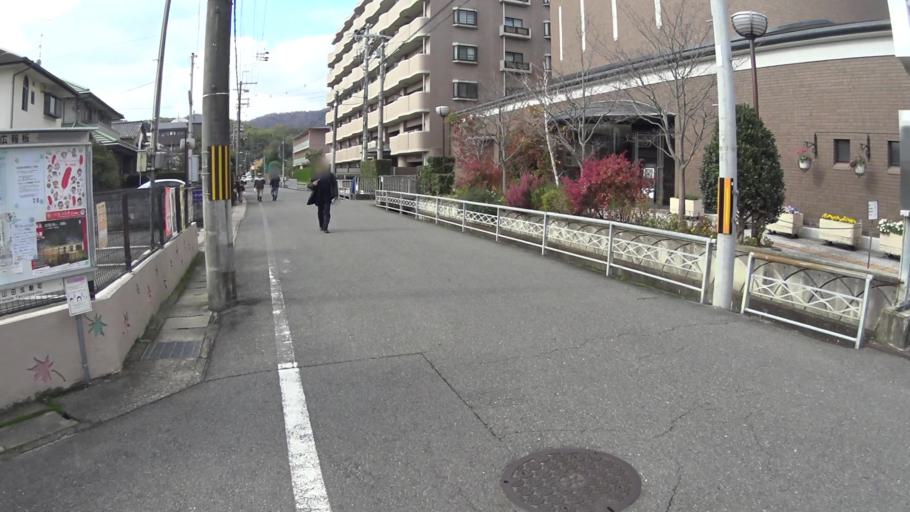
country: JP
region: Kyoto
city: Muko
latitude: 34.9896
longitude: 135.6915
